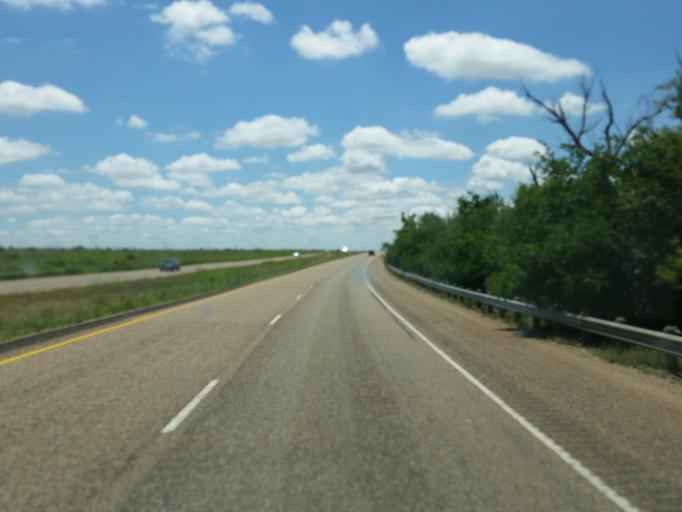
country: US
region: Texas
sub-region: Garza County
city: Post
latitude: 33.1066
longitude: -101.2654
